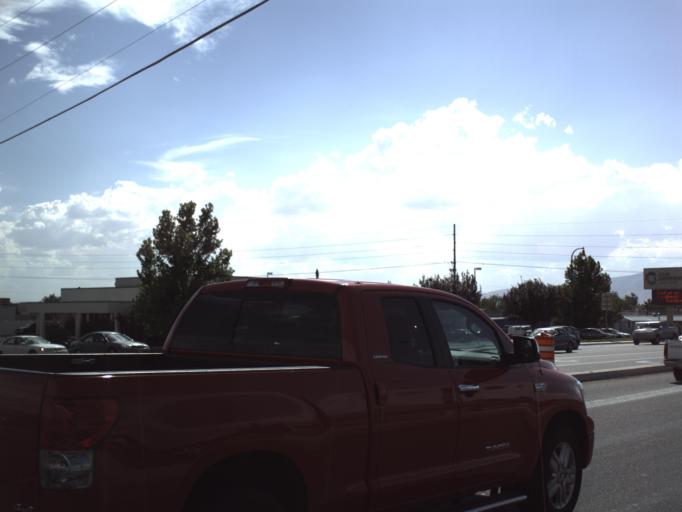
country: US
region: Utah
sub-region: Utah County
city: Orem
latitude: 40.3121
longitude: -111.6995
